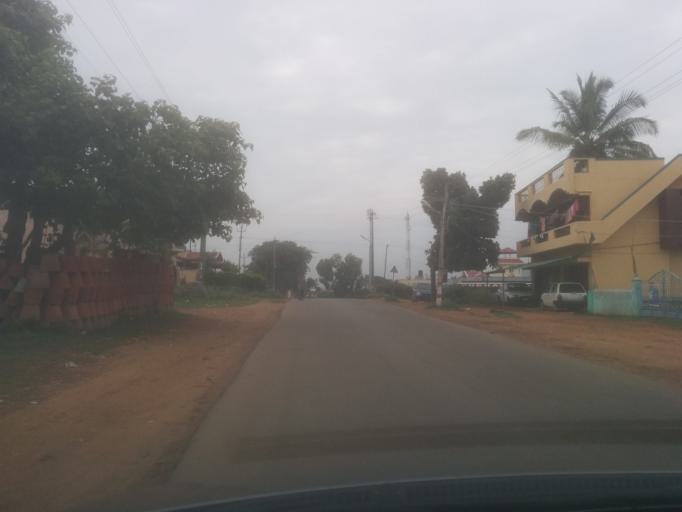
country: IN
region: Karnataka
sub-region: Chikmagalur
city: Chikmagalur
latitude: 13.3442
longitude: 75.7668
